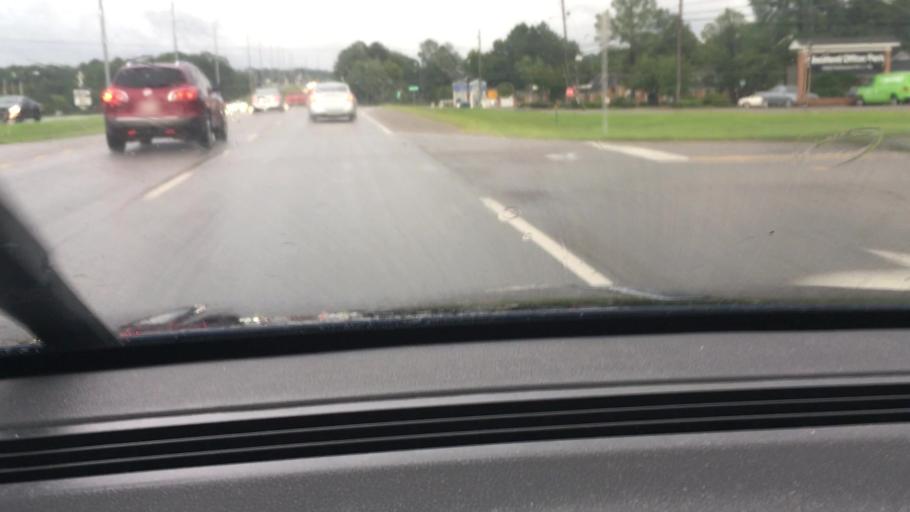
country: US
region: Alabama
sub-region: Tuscaloosa County
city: Northport
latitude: 33.2352
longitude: -87.5509
